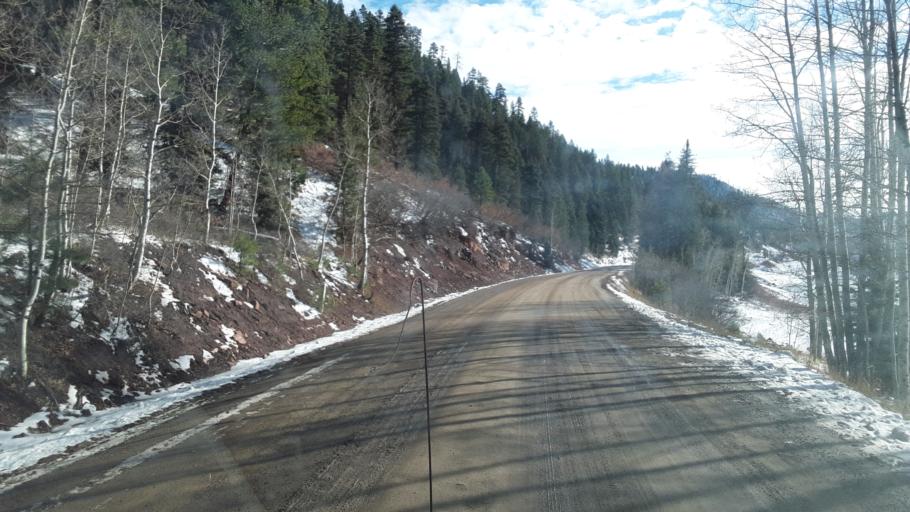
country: US
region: Colorado
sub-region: La Plata County
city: Bayfield
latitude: 37.3926
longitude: -107.6569
